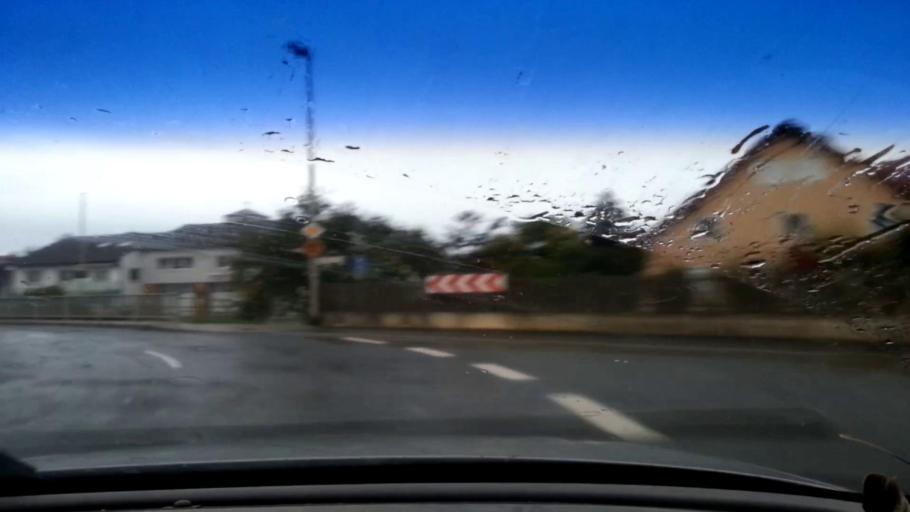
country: DE
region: Bavaria
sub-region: Upper Franconia
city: Walsdorf
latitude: 49.8708
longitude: 10.7801
